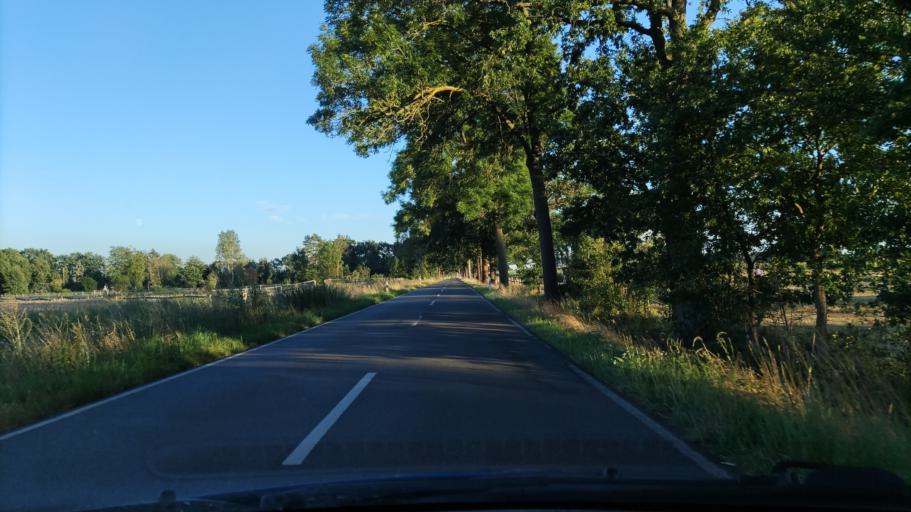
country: DE
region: Lower Saxony
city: Luechow
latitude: 52.9980
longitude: 11.1527
